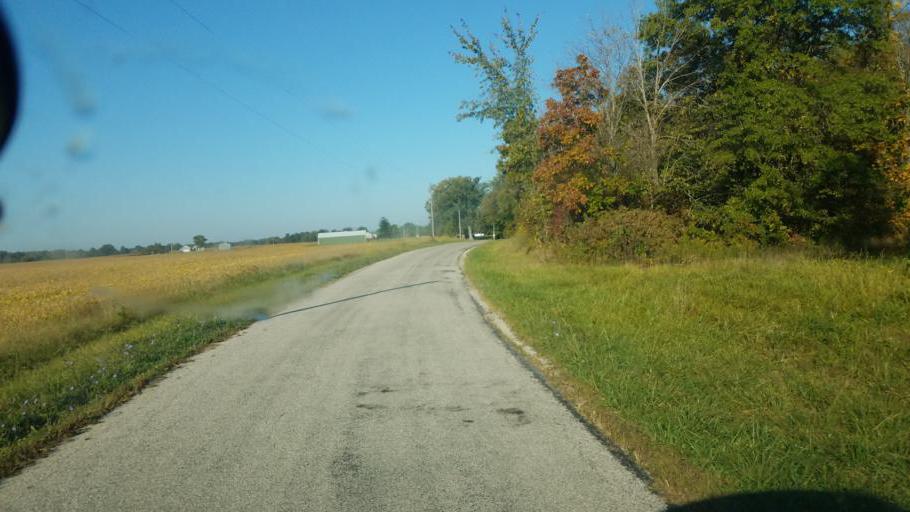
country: US
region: Ohio
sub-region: Marion County
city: Prospect
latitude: 40.5322
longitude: -83.2370
